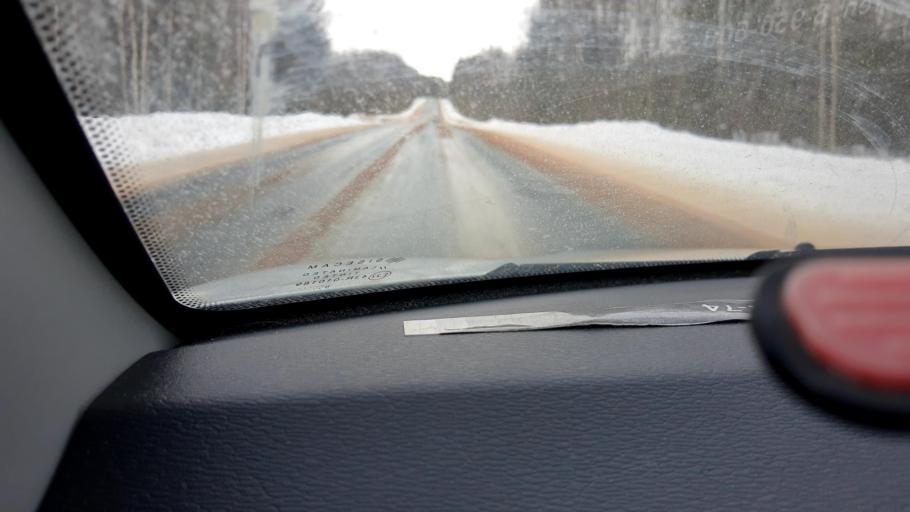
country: RU
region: Nizjnij Novgorod
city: Tonkino
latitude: 57.2931
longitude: 46.4623
